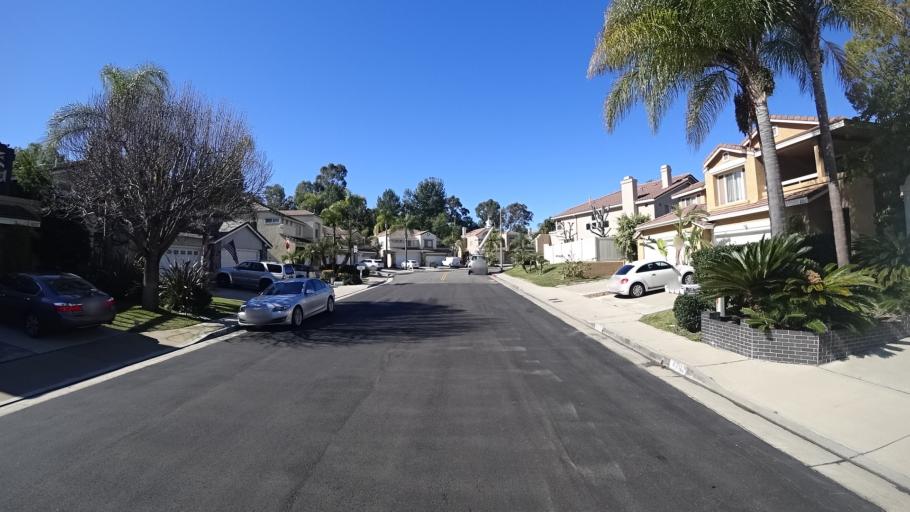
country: US
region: California
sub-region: Orange County
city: Yorba Linda
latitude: 33.8563
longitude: -117.7342
